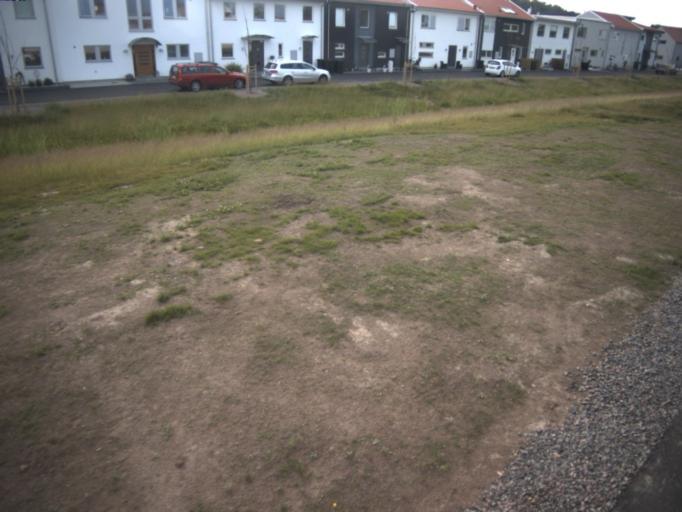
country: SE
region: Skane
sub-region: Helsingborg
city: Helsingborg
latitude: 56.0881
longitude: 12.6934
